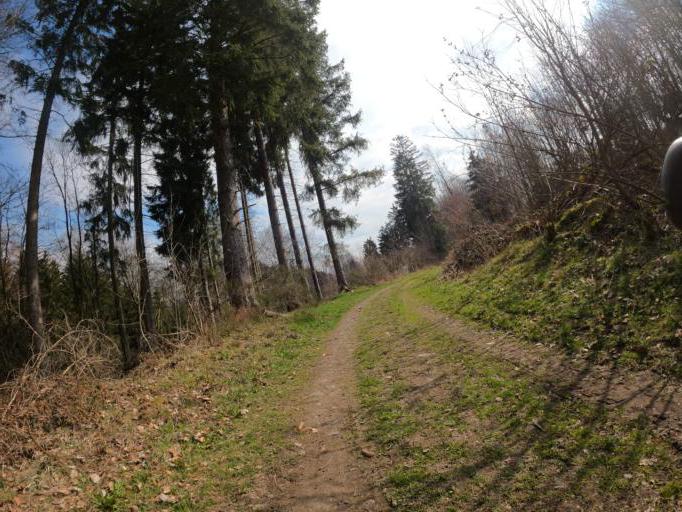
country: DE
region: North Rhine-Westphalia
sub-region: Regierungsbezirk Koln
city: Simmerath
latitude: 50.5958
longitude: 6.3044
